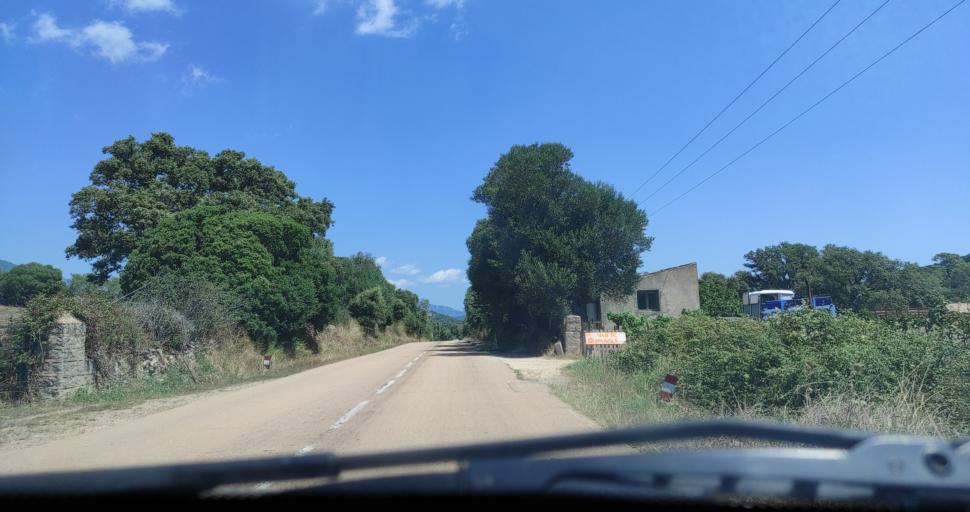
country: FR
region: Corsica
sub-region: Departement de la Corse-du-Sud
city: Porto-Vecchio
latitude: 41.5421
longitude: 9.1785
